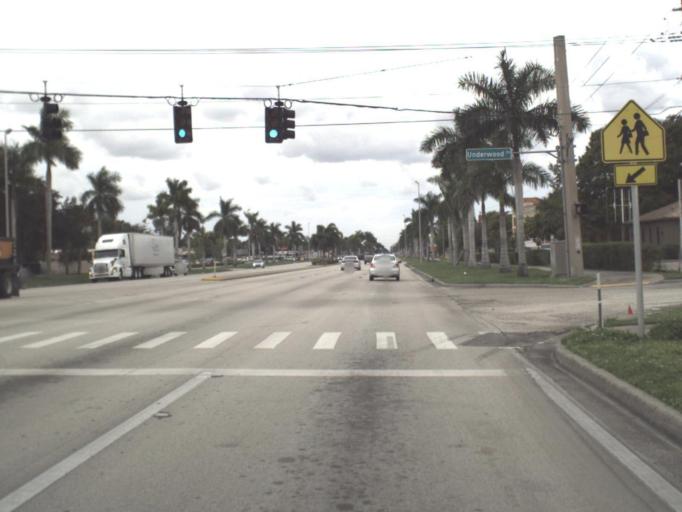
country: US
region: Florida
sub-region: Lee County
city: Tice
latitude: 26.6800
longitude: -81.8062
